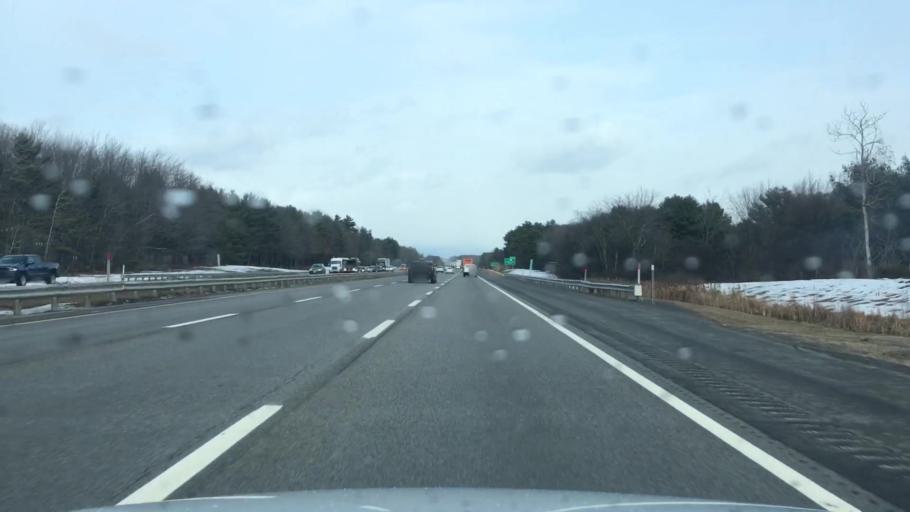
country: US
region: Maine
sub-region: Cumberland County
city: West Scarborough
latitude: 43.5746
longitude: -70.4028
